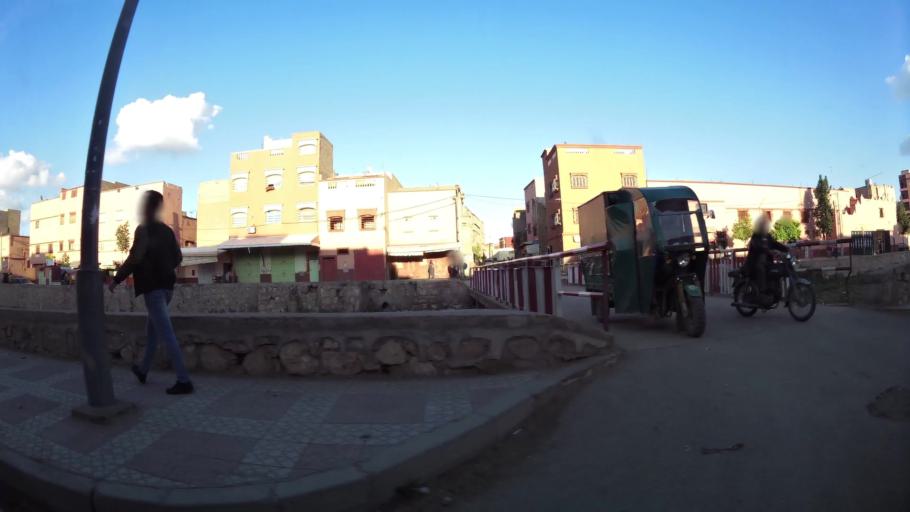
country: MA
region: Marrakech-Tensift-Al Haouz
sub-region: Kelaa-Des-Sraghna
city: Sidi Abdallah
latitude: 32.2410
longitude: -7.9491
